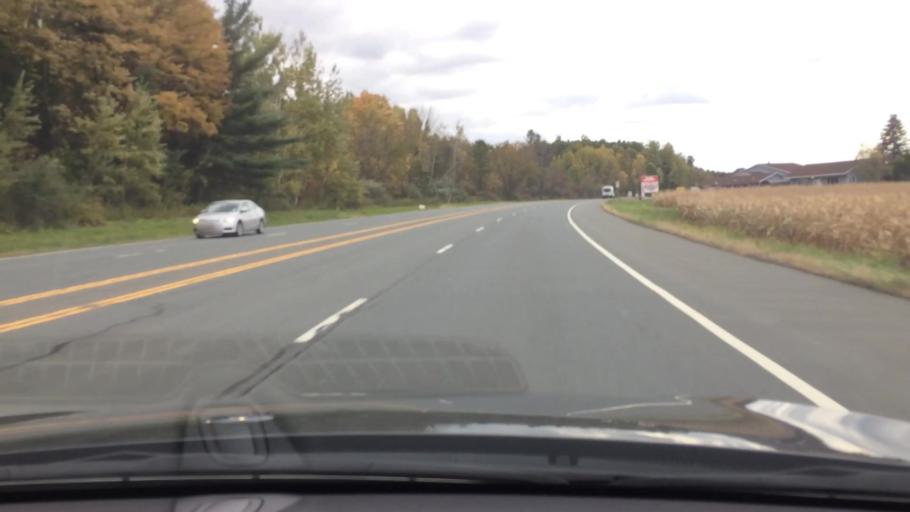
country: US
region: New York
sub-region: Columbia County
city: Niverville
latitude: 42.4799
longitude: -73.6800
